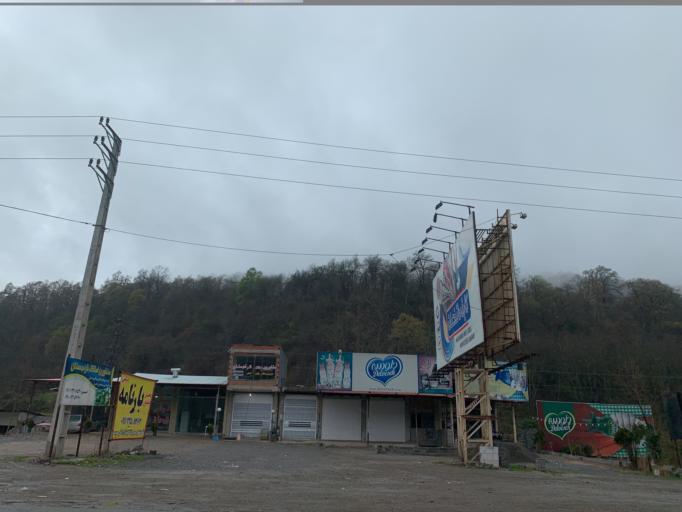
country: IR
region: Mazandaran
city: Amol
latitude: 36.3727
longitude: 52.3534
